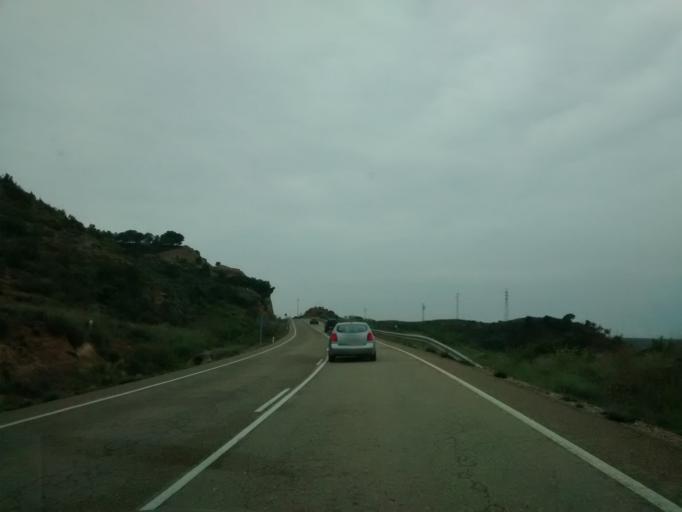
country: ES
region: Aragon
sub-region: Provincia de Zaragoza
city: Caspe
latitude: 41.2661
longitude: -0.0544
